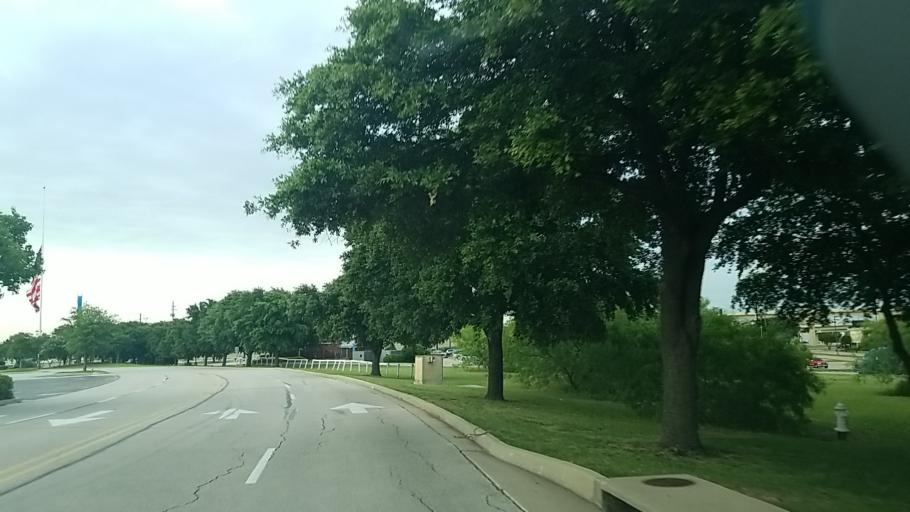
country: US
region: Texas
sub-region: Denton County
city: Lewisville
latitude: 33.0015
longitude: -96.9678
